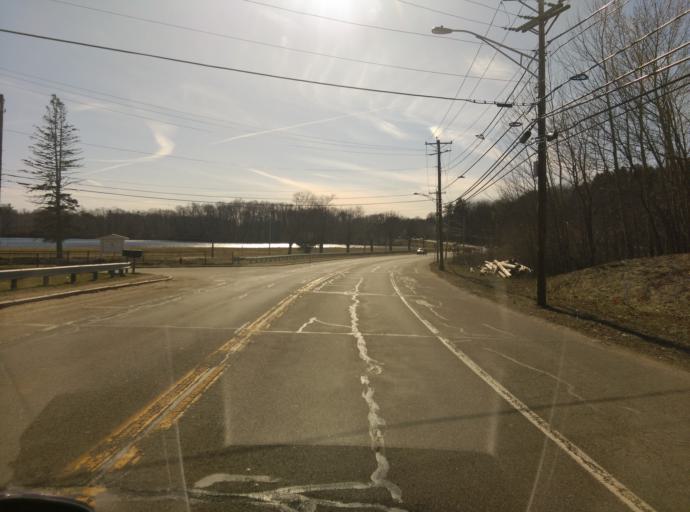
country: US
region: Massachusetts
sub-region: Essex County
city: Haverhill
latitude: 42.7952
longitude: -71.0614
